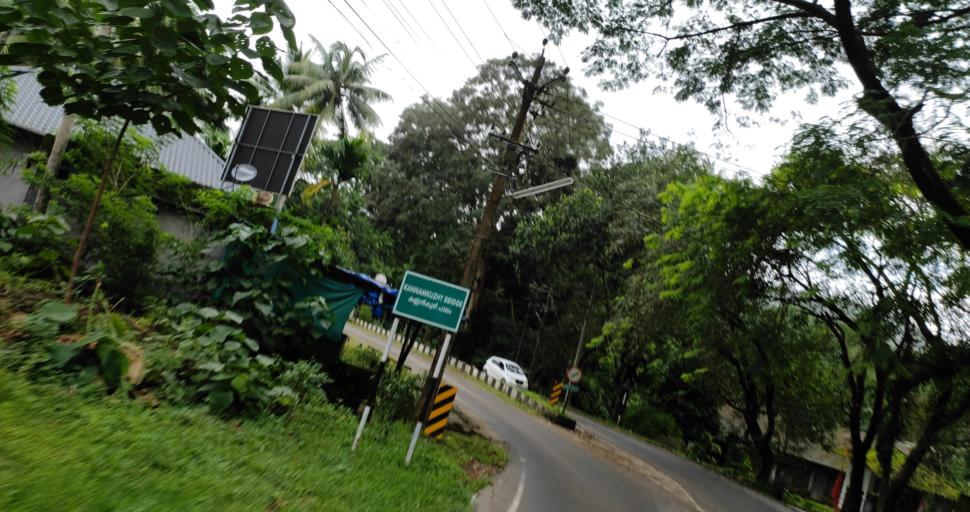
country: IN
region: Kerala
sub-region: Ernakulam
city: Angamali
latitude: 10.2872
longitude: 76.5561
